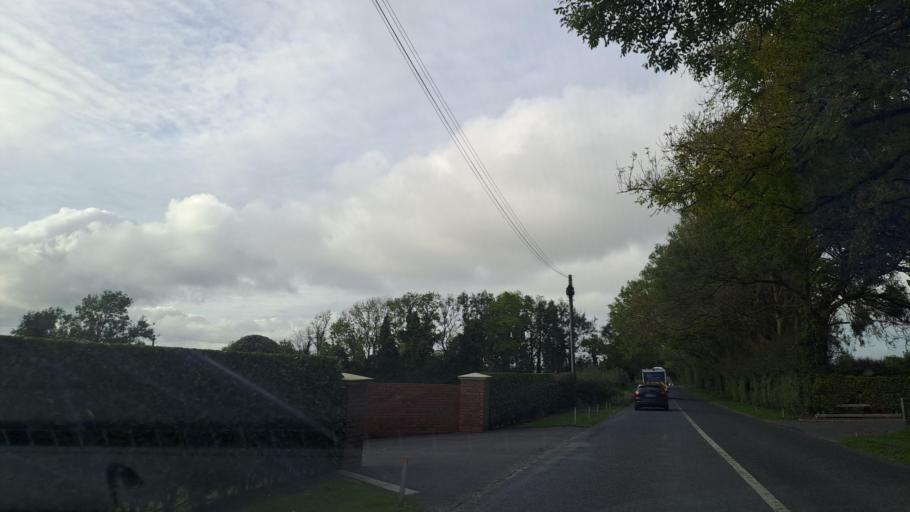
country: IE
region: Leinster
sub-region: An Mhi
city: Navan
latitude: 53.7230
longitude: -6.7025
